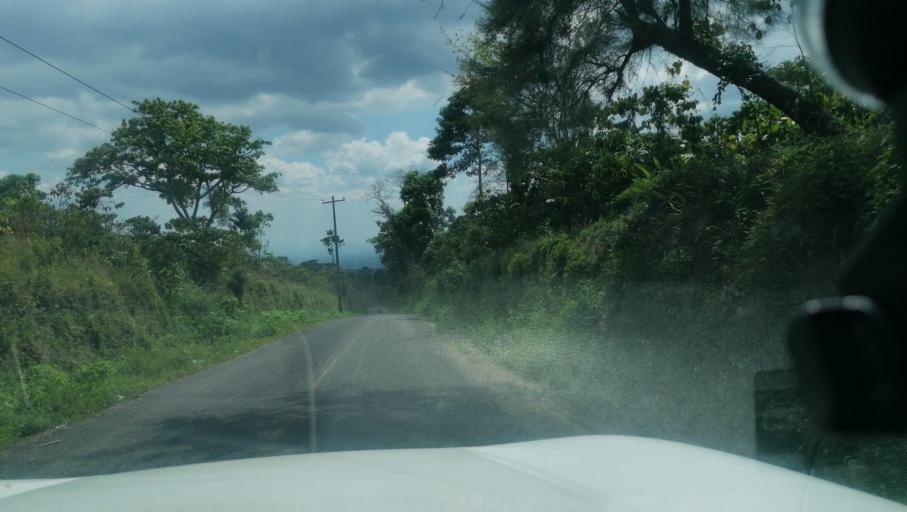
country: MX
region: Chiapas
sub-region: Cacahoatan
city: Benito Juarez
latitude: 15.0534
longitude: -92.1520
